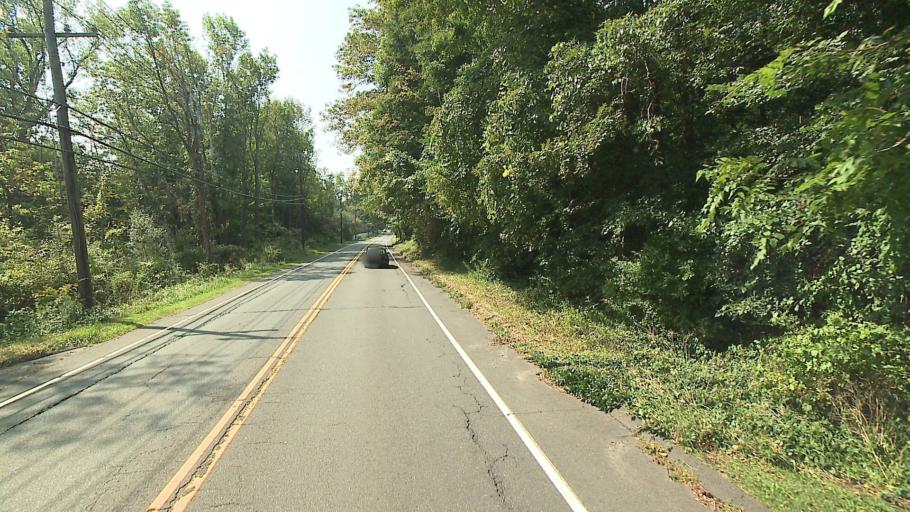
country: US
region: Connecticut
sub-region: Fairfield County
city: Ridgefield
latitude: 41.3145
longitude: -73.4811
